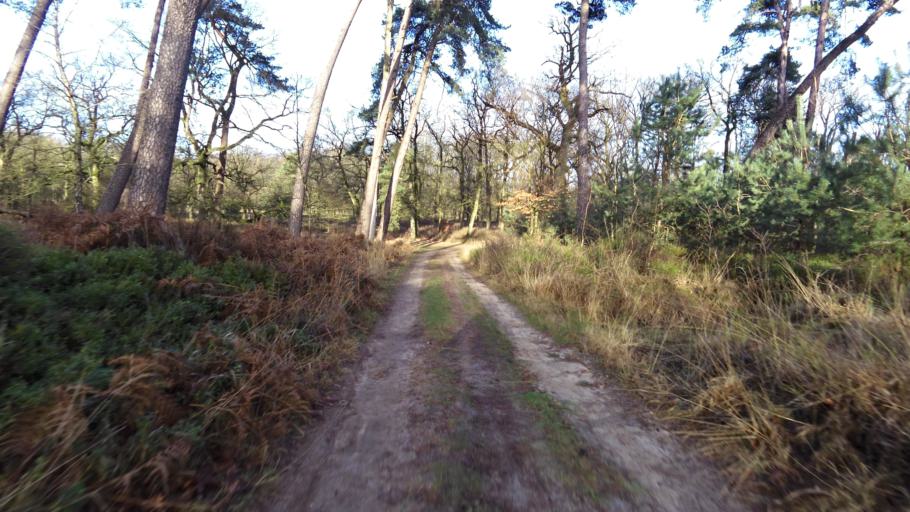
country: NL
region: Gelderland
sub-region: Gemeente Epe
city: Vaassen
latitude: 52.2452
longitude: 5.8806
